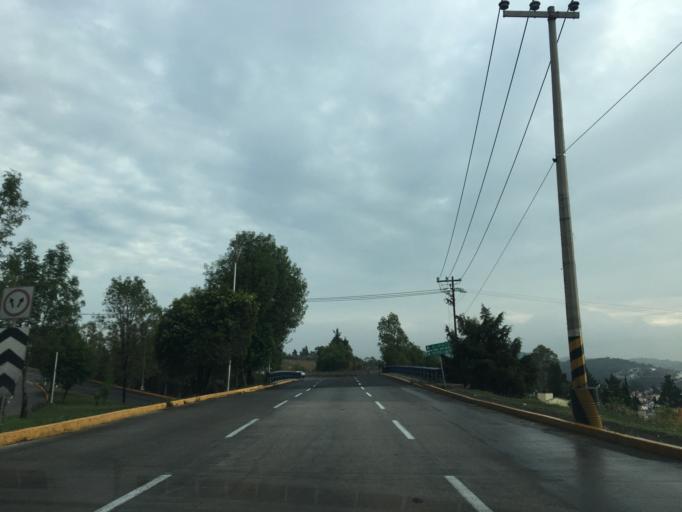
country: MX
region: Mexico
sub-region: Naucalpan de Juarez
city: Rincon Verde
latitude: 19.5149
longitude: -99.2654
